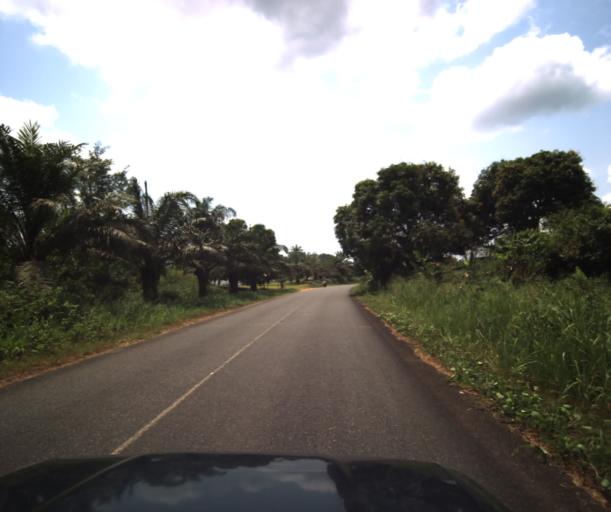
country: CM
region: Centre
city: Eseka
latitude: 3.7988
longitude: 10.8188
